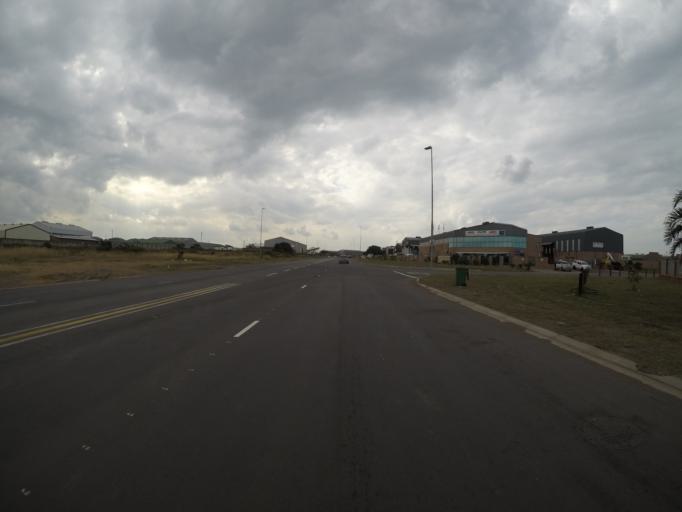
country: ZA
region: KwaZulu-Natal
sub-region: uThungulu District Municipality
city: Richards Bay
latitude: -28.7401
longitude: 32.0364
